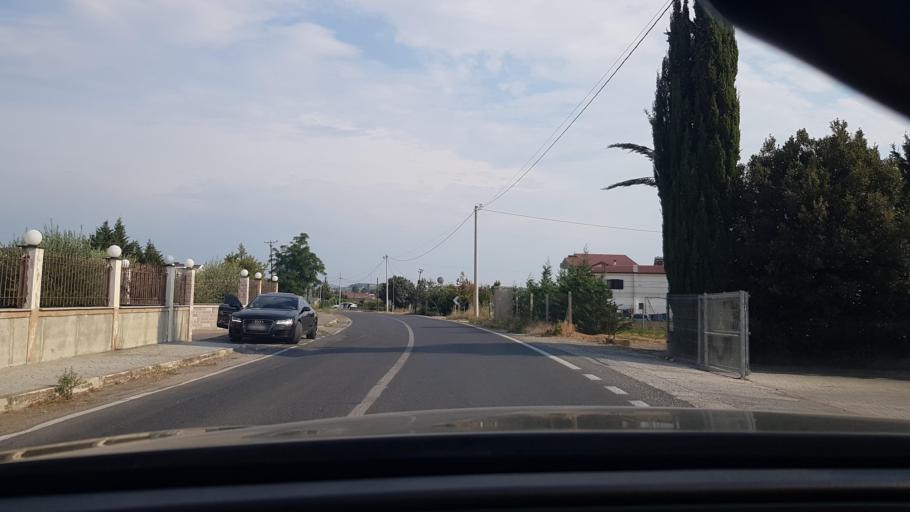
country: AL
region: Durres
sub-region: Rrethi i Durresit
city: Manze
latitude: 41.4649
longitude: 19.5625
